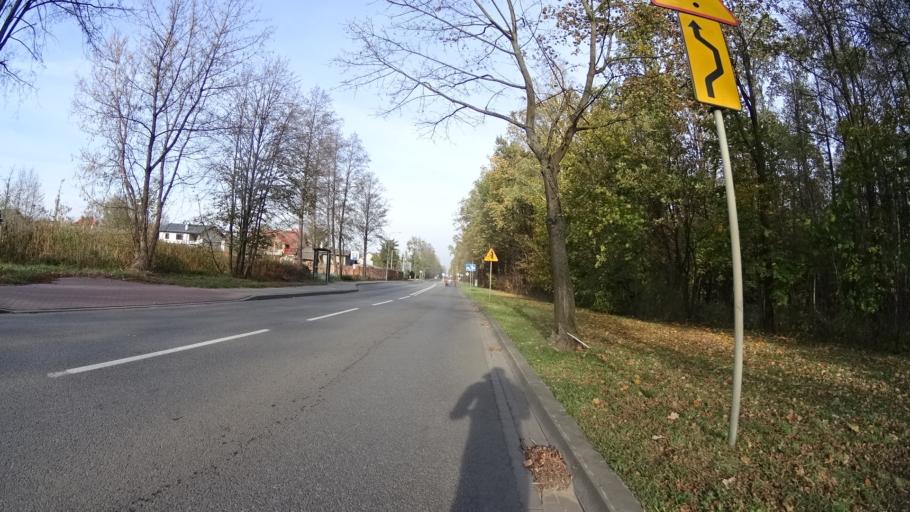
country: PL
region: Masovian Voivodeship
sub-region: Powiat warszawski zachodni
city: Babice
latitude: 52.2637
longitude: 20.8561
